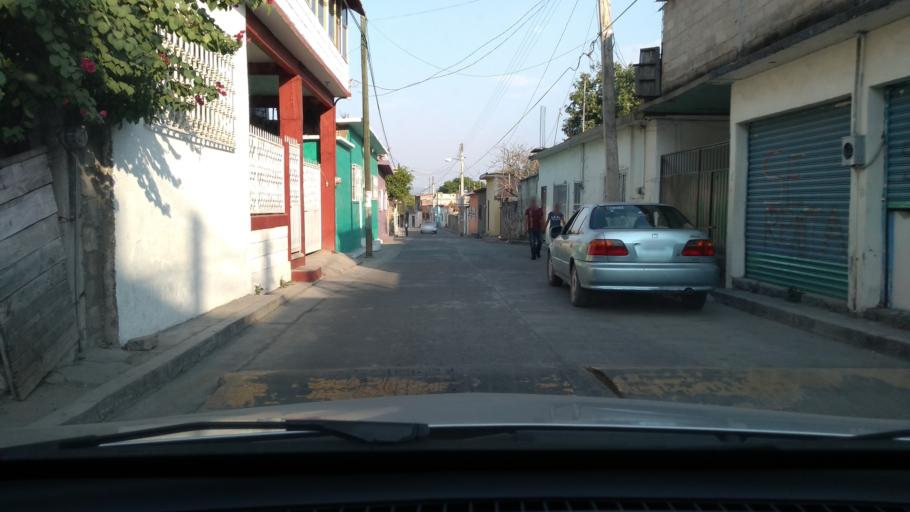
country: MX
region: Morelos
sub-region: Jojutla
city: Tehuixtla
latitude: 18.5612
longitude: -99.2743
